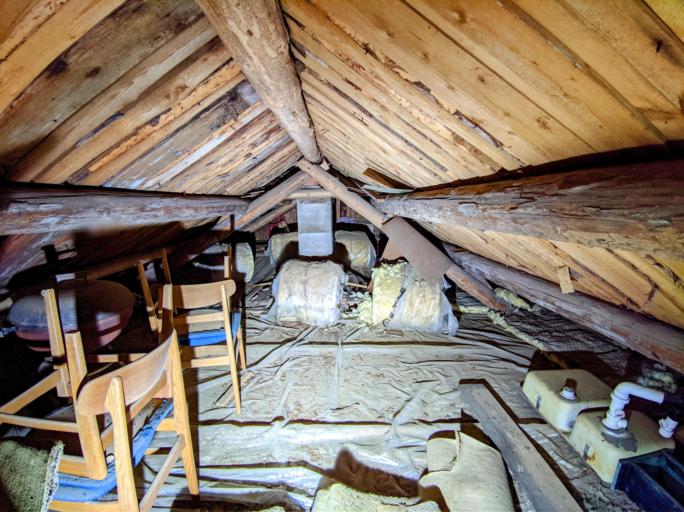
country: NO
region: Akershus
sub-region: Nittedal
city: Aneby
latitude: 60.0741
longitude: 10.9038
